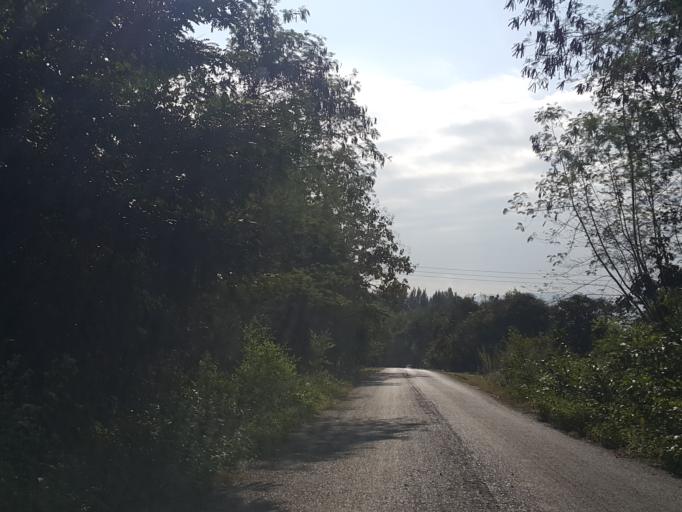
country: TH
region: Lampang
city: Mae Mo
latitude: 18.2950
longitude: 99.6703
